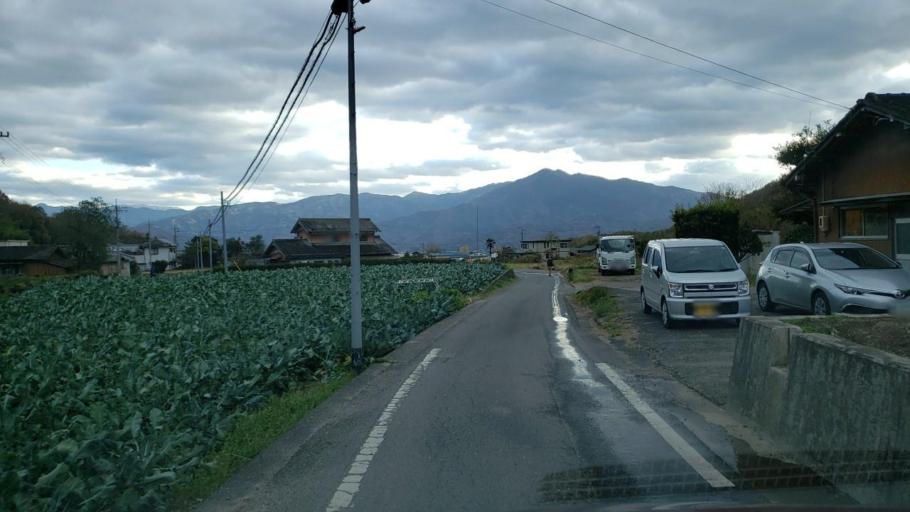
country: JP
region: Tokushima
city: Wakimachi
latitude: 34.1074
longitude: 134.2242
